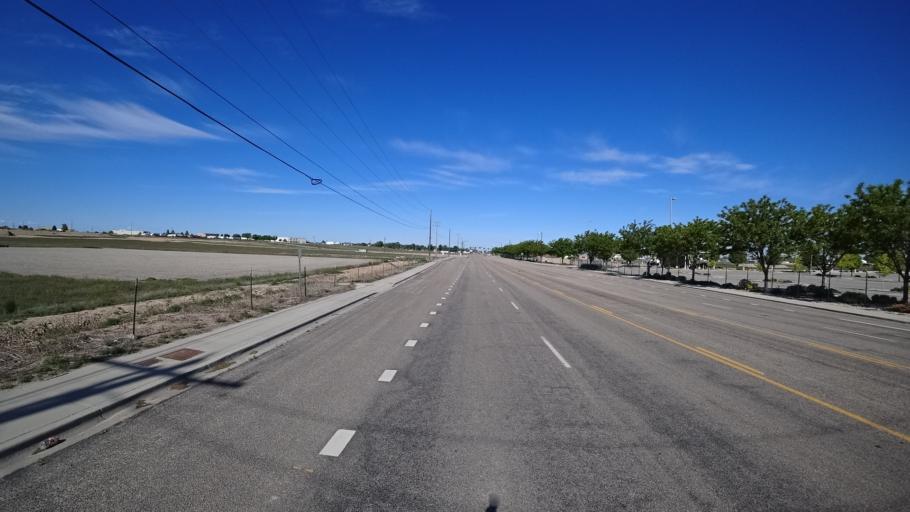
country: US
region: Idaho
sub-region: Ada County
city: Garden City
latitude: 43.5752
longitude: -116.2502
